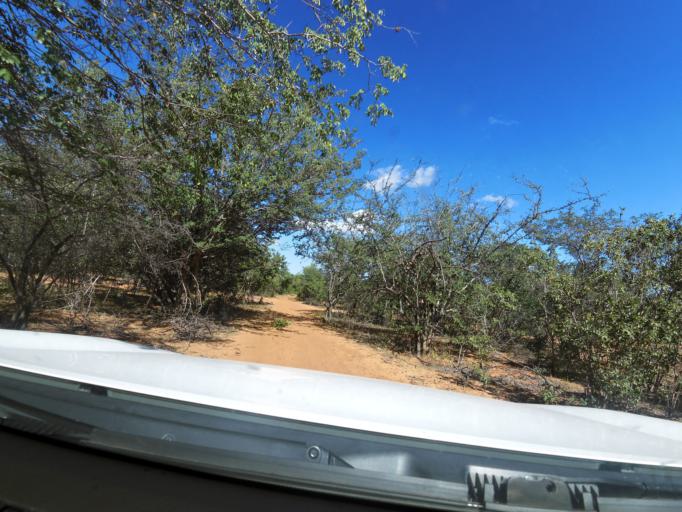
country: ZW
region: Matabeleland North
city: Kamativi Mine
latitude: -17.9671
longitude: 27.1406
